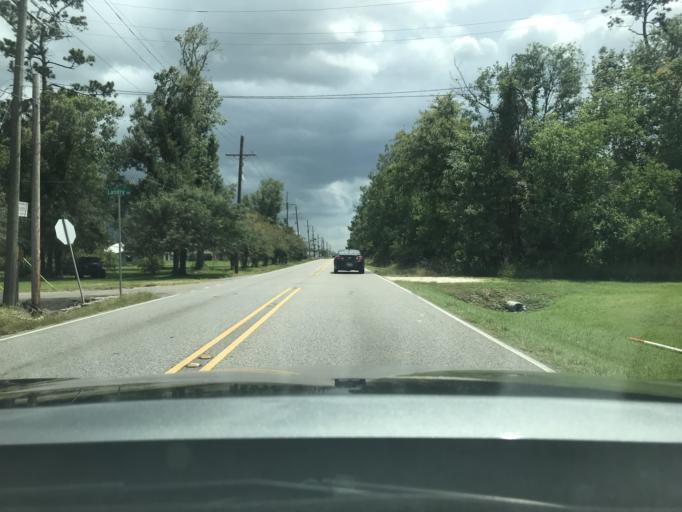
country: US
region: Louisiana
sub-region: Calcasieu Parish
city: Westlake
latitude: 30.2718
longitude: -93.2582
